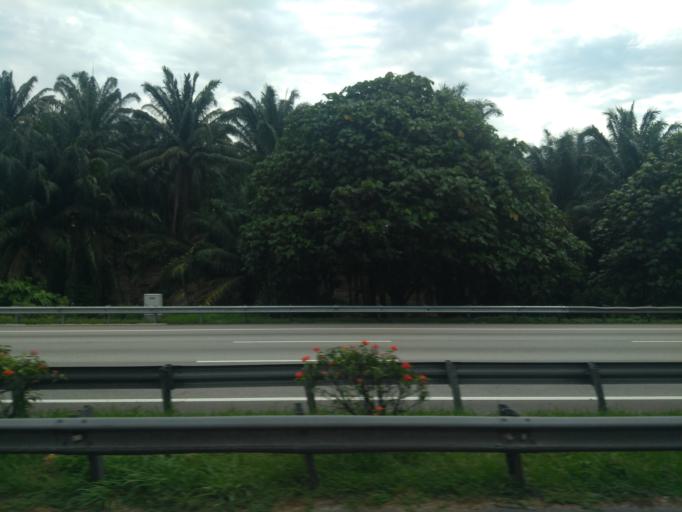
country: MY
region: Negeri Sembilan
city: Seremban
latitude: 2.6437
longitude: 101.9936
